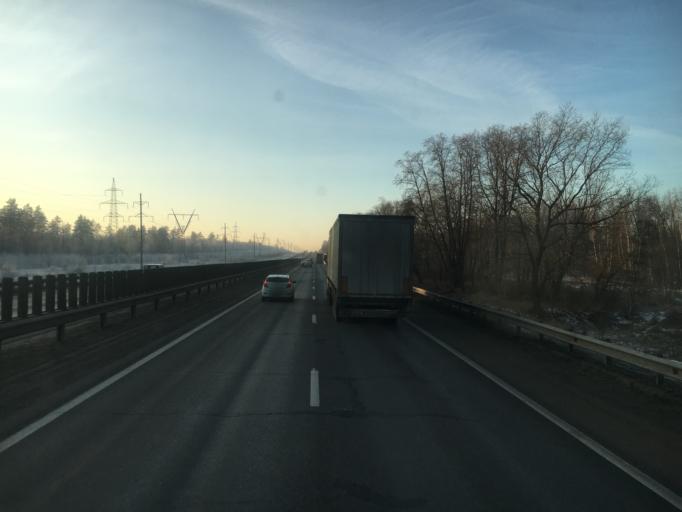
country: RU
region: Samara
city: Pribrezhnyy
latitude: 53.5149
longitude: 49.8843
